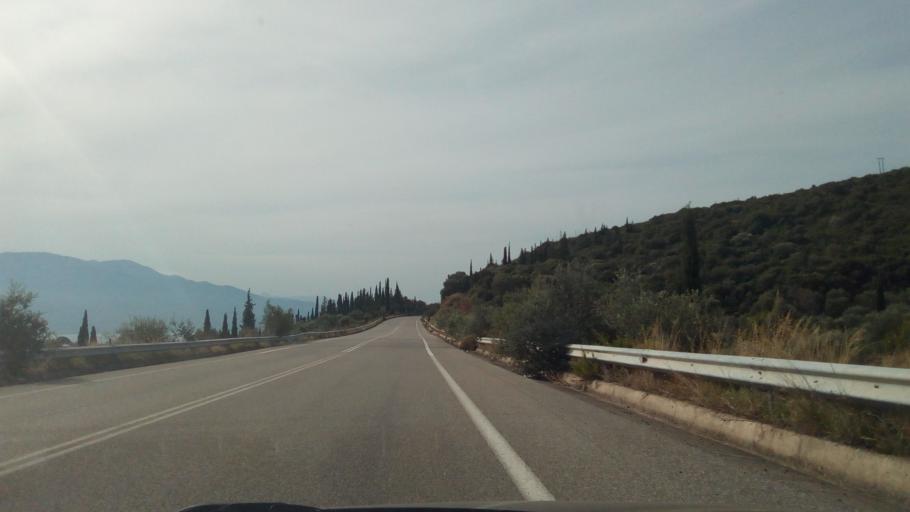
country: GR
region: West Greece
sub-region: Nomos Aitolias kai Akarnanias
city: Nafpaktos
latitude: 38.3893
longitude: 21.7967
